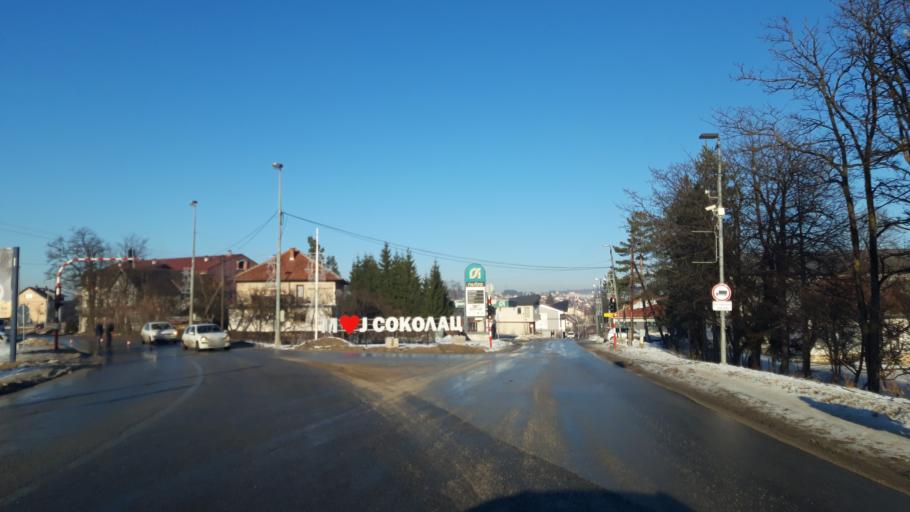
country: BA
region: Republika Srpska
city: Sokolac
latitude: 43.9317
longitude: 18.7902
